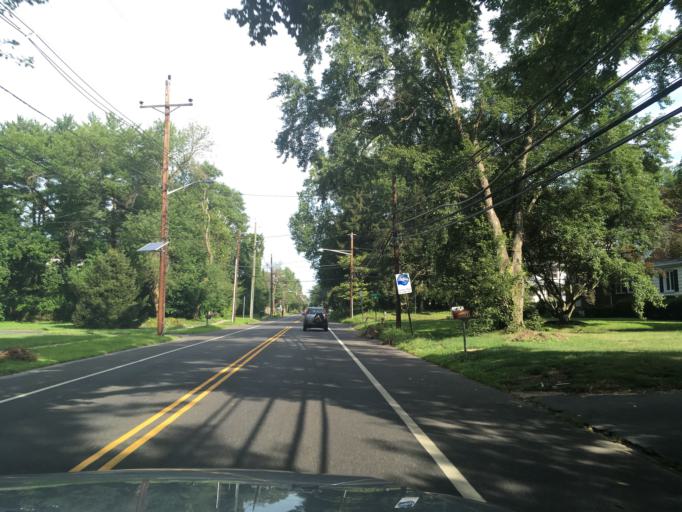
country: US
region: New Jersey
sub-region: Mercer County
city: Princeton Junction
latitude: 40.3244
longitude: -74.6287
